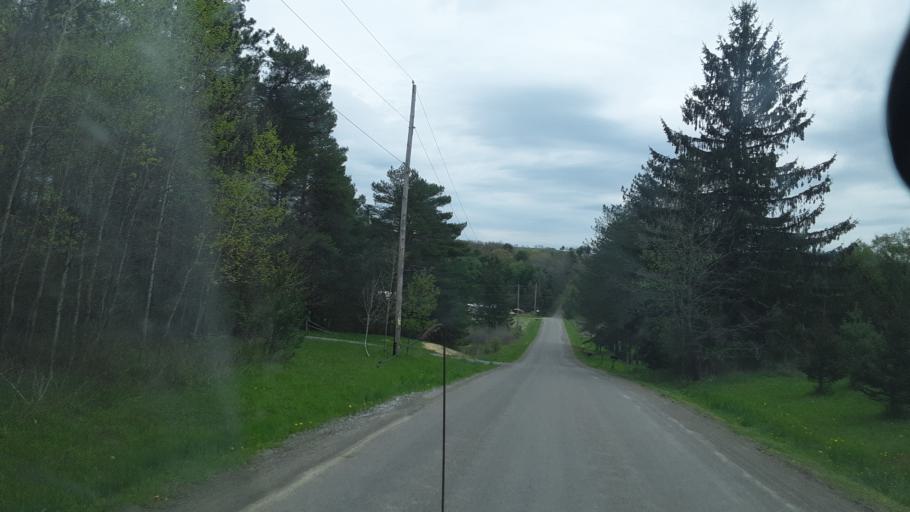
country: US
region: New York
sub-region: Steuben County
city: Addison
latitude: 42.0930
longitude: -77.3070
